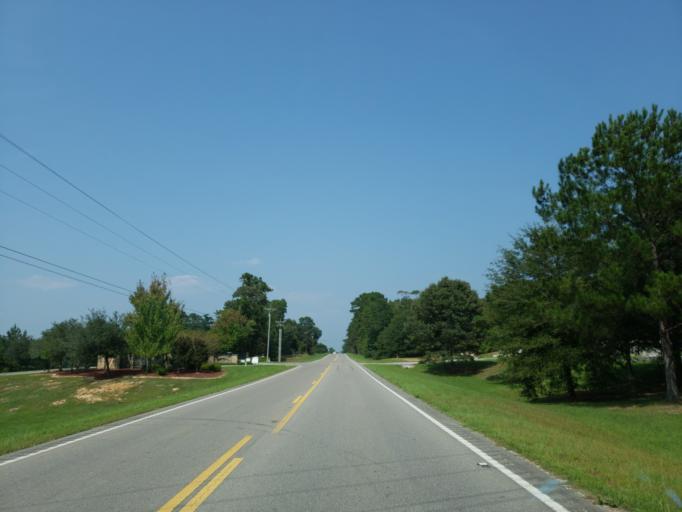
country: US
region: Mississippi
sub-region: Jones County
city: Ellisville
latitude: 31.5505
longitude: -89.2529
